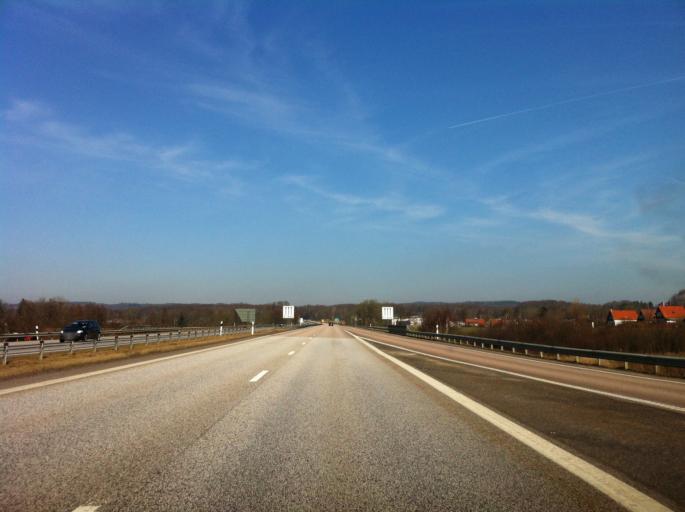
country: SE
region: Skane
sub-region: Angelholms Kommun
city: Munka-Ljungby
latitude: 56.3153
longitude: 12.9122
